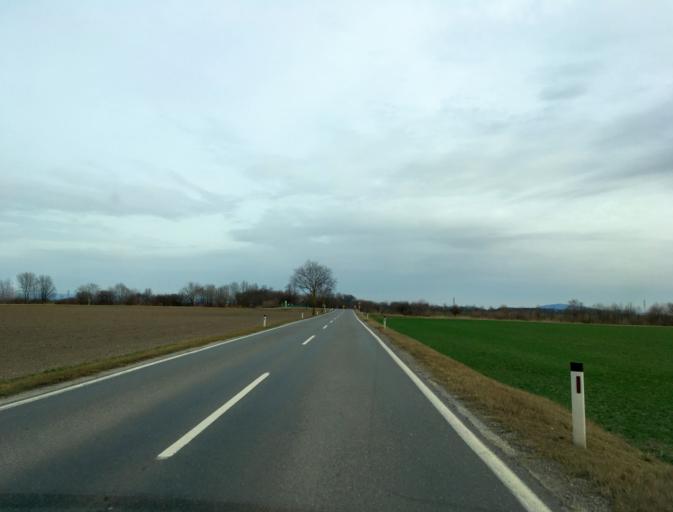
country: AT
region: Lower Austria
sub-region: Politischer Bezirk Ganserndorf
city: Leopoldsdorf im Marchfelde
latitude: 48.2269
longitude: 16.7143
